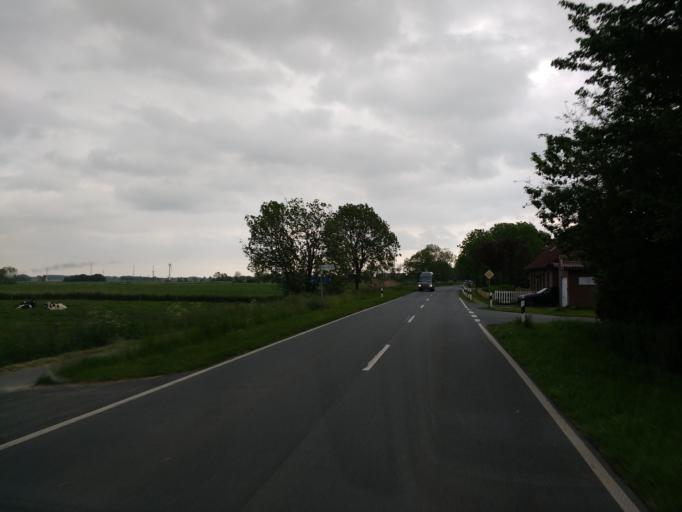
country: DE
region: Lower Saxony
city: Schillig
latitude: 53.6504
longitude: 7.9948
